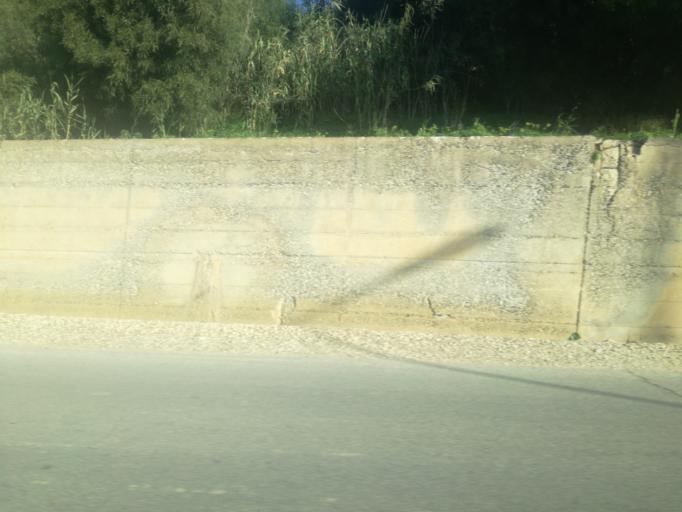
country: IT
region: Sicily
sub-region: Provincia di Caltanissetta
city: Gela
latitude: 37.0684
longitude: 14.2272
